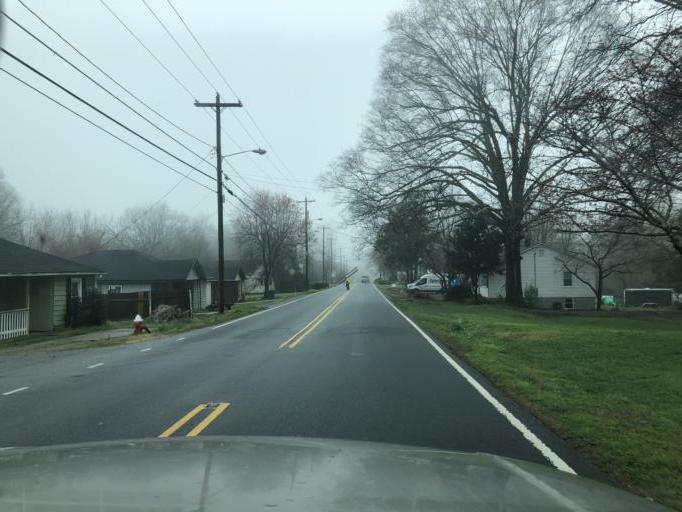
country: US
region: North Carolina
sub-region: Gaston County
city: Cherryville
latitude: 35.3789
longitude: -81.3899
